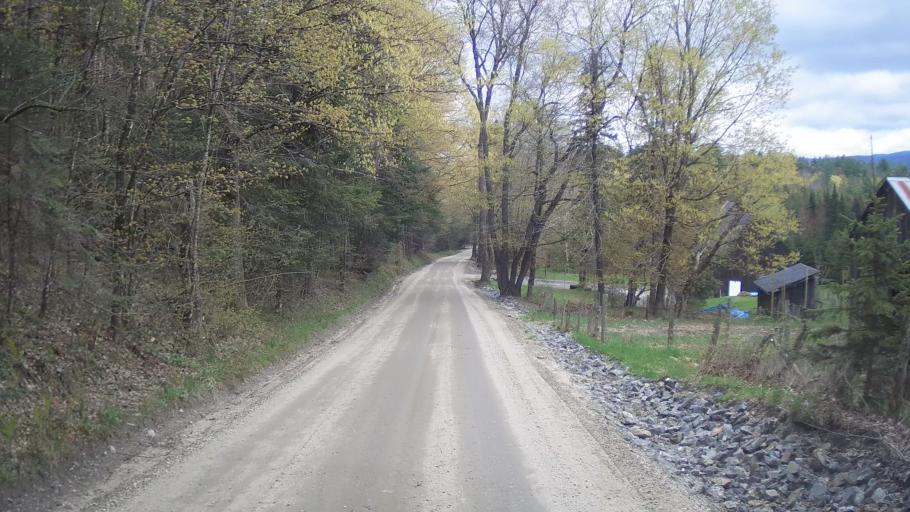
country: US
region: Vermont
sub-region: Caledonia County
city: Lyndonville
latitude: 44.6126
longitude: -71.9443
